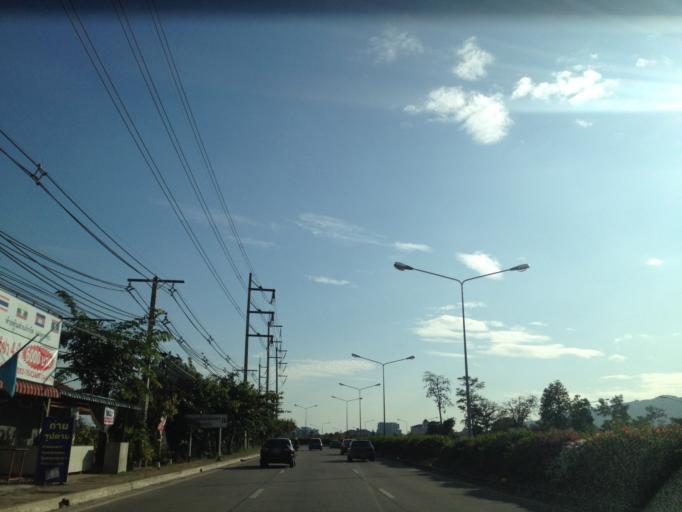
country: TH
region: Chiang Mai
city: Chiang Mai
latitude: 18.8333
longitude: 98.9637
